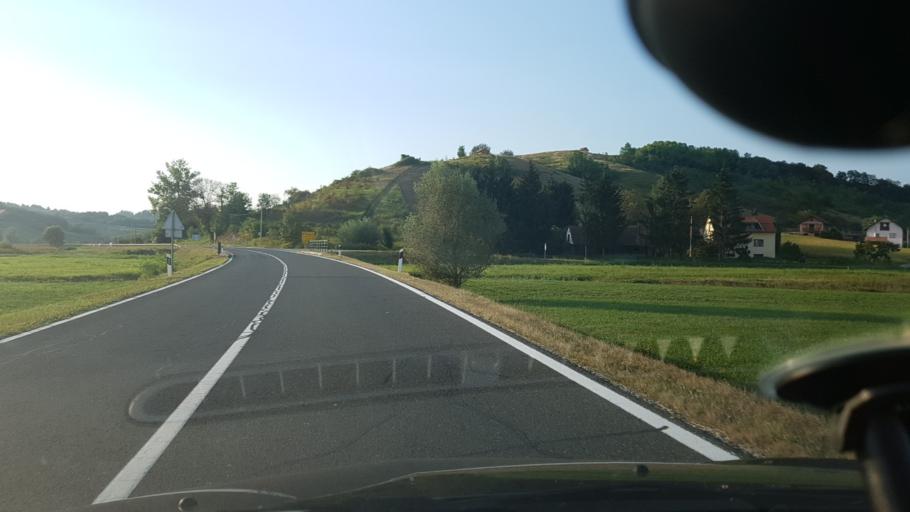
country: HR
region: Krapinsko-Zagorska
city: Pregrada
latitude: 46.1122
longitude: 15.8122
